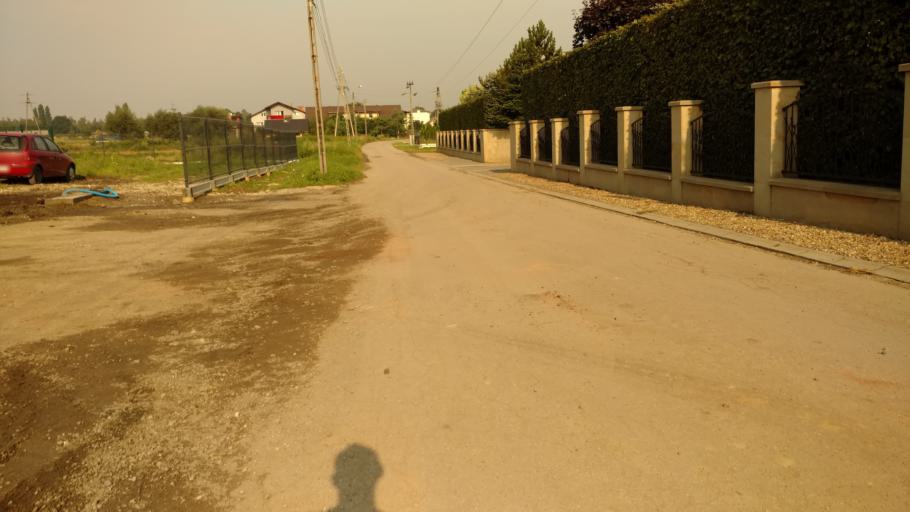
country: PL
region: Silesian Voivodeship
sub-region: Powiat pszczynski
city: Piasek
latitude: 50.0032
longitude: 18.9665
